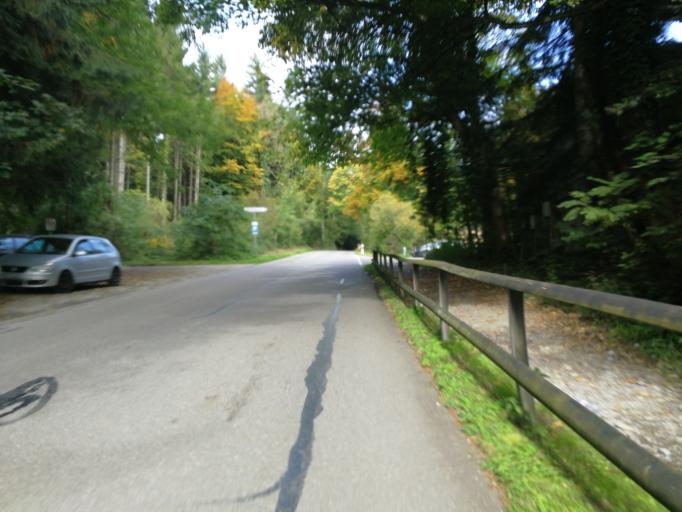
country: CH
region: Zurich
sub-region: Bezirk Meilen
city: Oetwil am See
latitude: 47.2650
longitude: 8.7122
